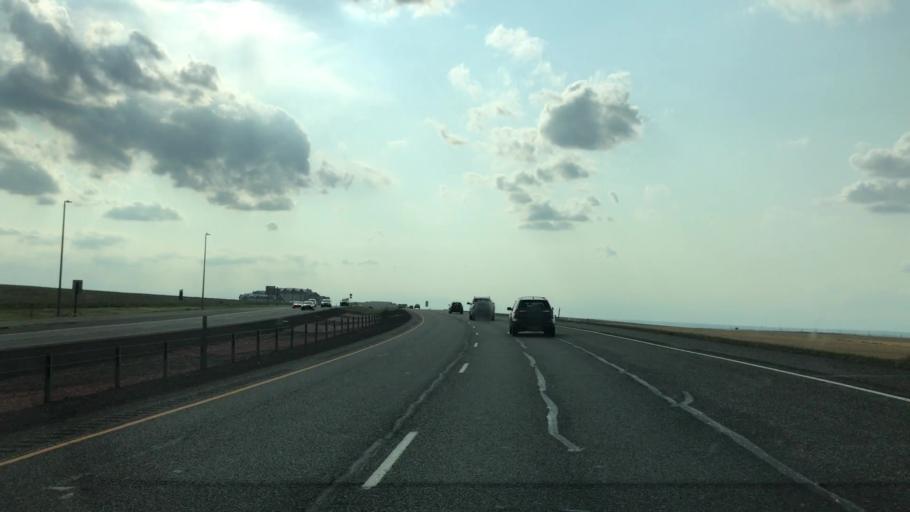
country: US
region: Colorado
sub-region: Adams County
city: Aurora
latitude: 39.8168
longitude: -104.7259
